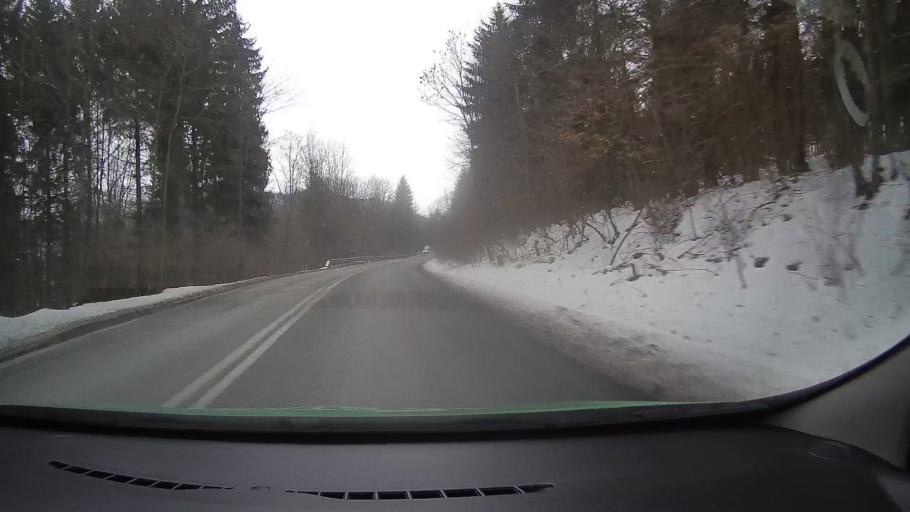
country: RO
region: Brasov
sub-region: Oras Predeal
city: Predeal
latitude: 45.5205
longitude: 25.5069
